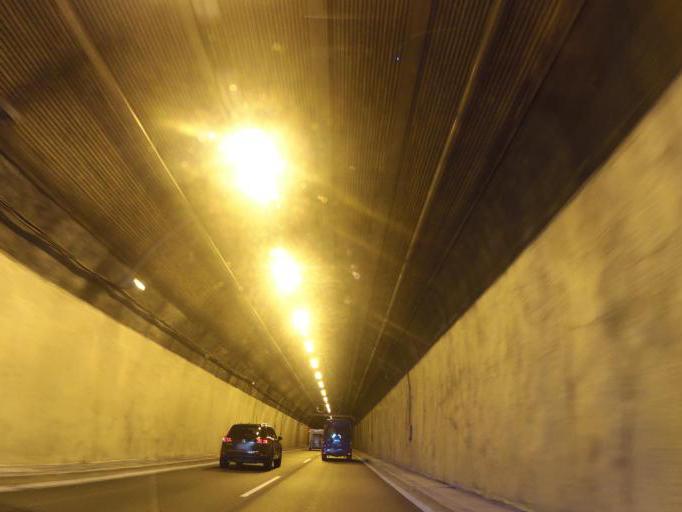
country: DE
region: Baden-Wuerttemberg
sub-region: Regierungsbezirk Stuttgart
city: Wiesensteig
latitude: 48.5507
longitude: 9.6351
